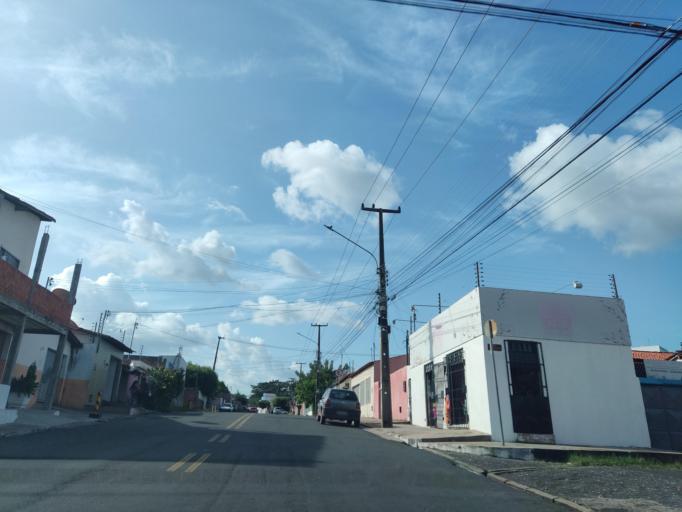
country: BR
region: Piaui
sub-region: Teresina
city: Teresina
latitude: -5.0808
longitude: -42.8024
